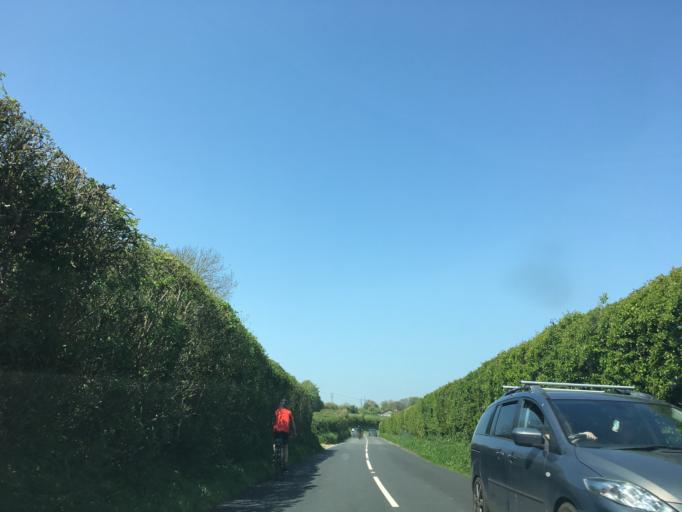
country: GB
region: England
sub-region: Isle of Wight
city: Niton
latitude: 50.5924
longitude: -1.2604
